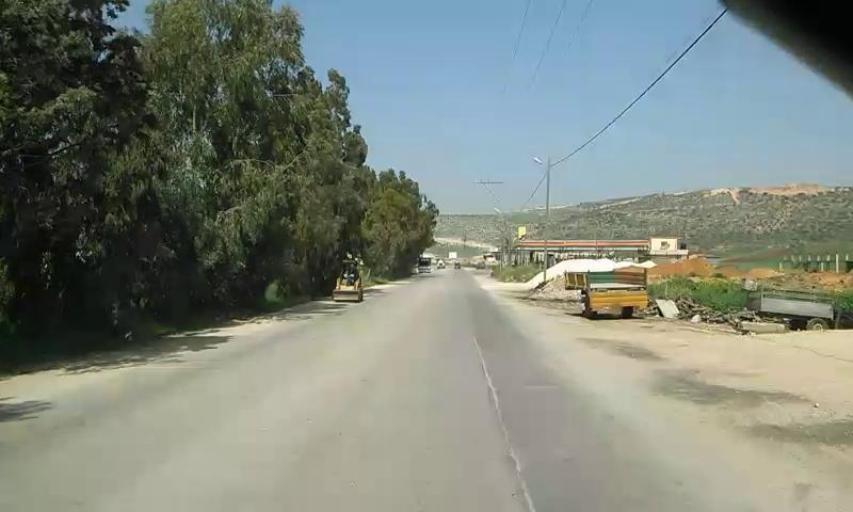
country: PS
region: West Bank
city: Az Zababidah
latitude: 32.3927
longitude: 35.3209
